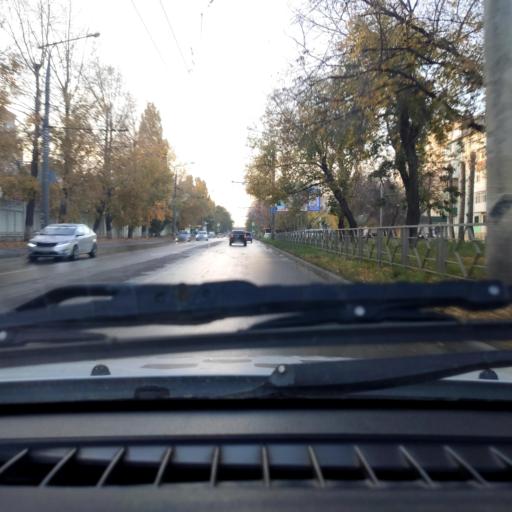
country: RU
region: Samara
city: Tol'yatti
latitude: 53.5140
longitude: 49.4293
